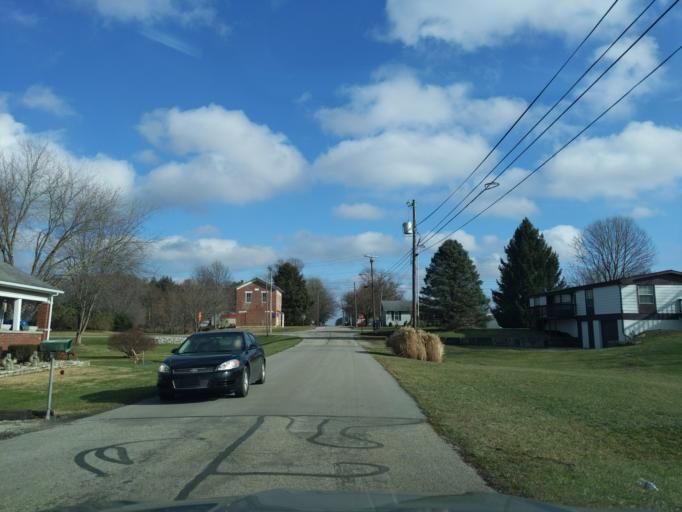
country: US
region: Indiana
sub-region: Ripley County
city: Batesville
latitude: 39.3093
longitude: -85.3269
